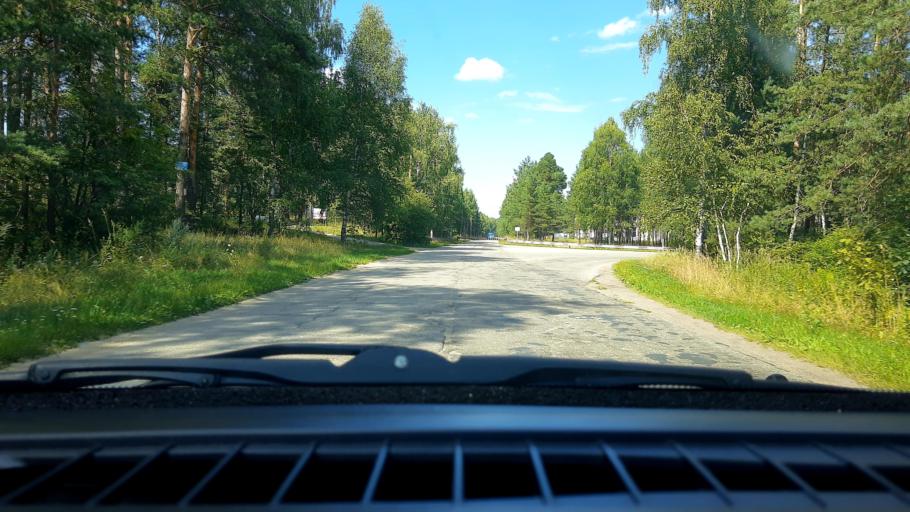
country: RU
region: Nizjnij Novgorod
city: Babino
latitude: 56.3298
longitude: 43.6342
